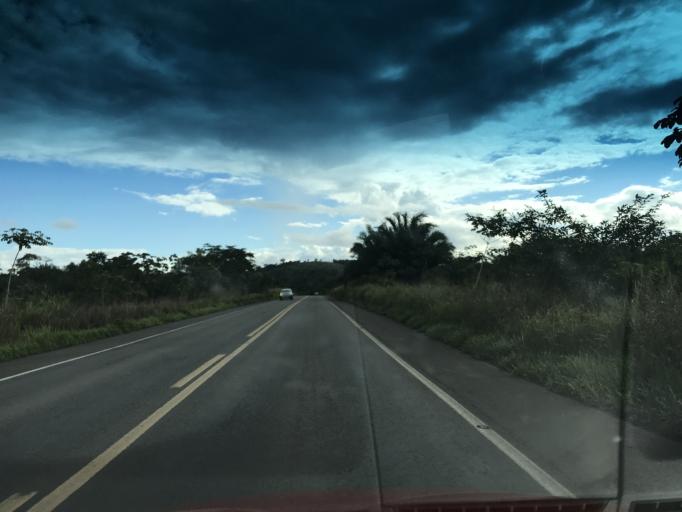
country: BR
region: Bahia
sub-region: Ibirapitanga
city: Ibirapitanga
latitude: -14.1510
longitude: -39.3405
